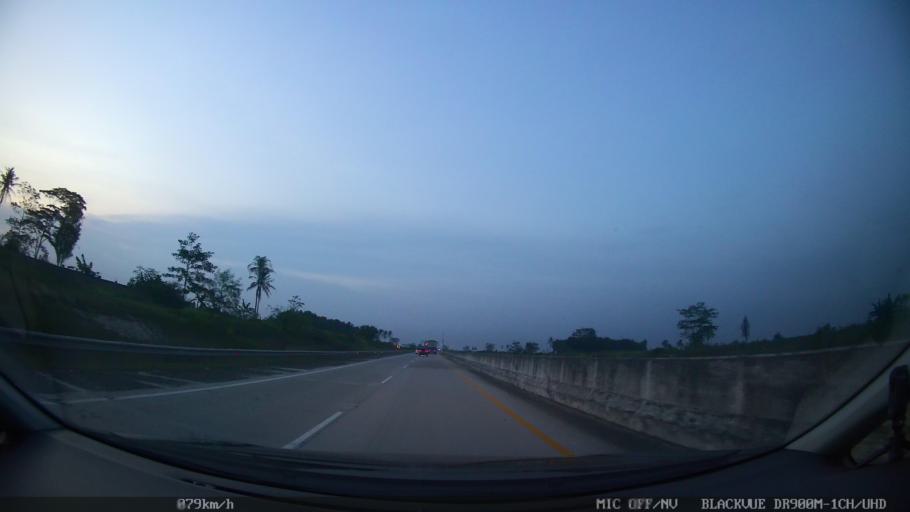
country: ID
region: Lampung
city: Sidorejo
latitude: -5.6223
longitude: 105.5632
